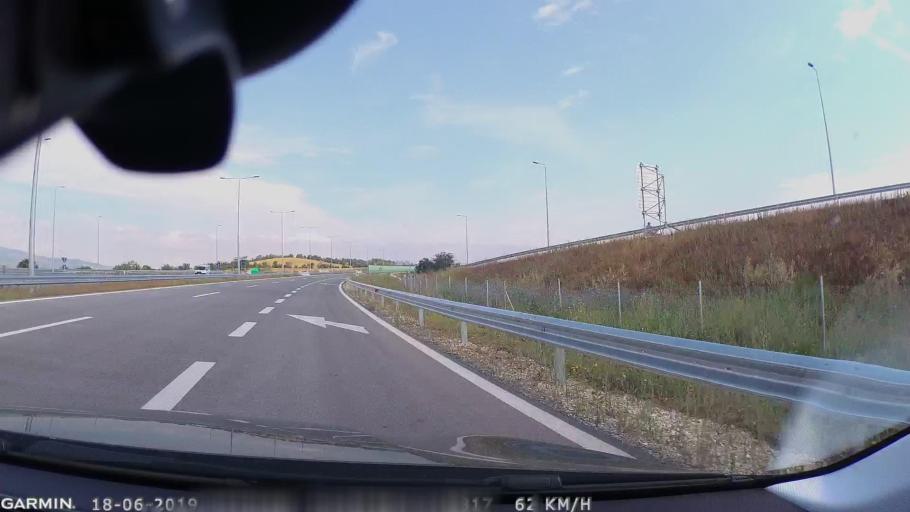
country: MK
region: Sveti Nikole
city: Sveti Nikole
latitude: 41.8778
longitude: 21.9378
